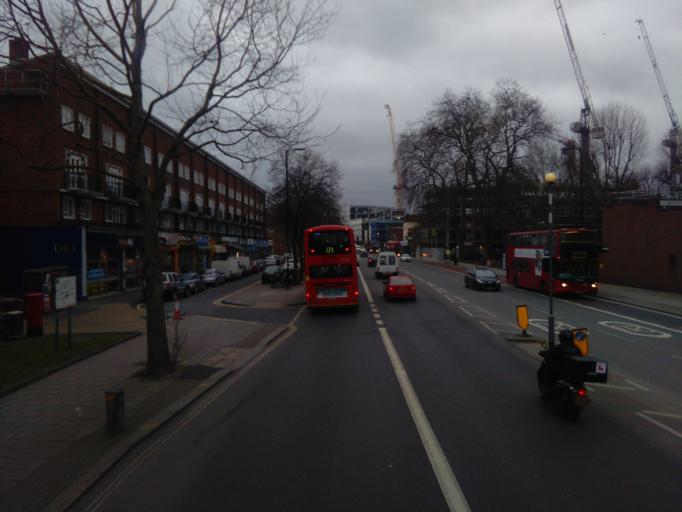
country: GB
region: England
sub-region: Greater London
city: Camberwell
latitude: 51.4784
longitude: -0.0939
